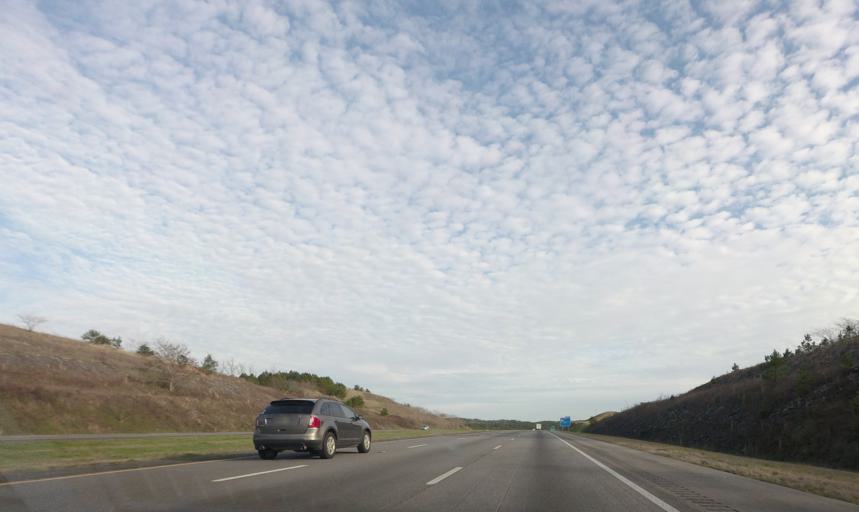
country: US
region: Alabama
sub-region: Walker County
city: Dora
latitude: 33.6822
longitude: -87.0935
